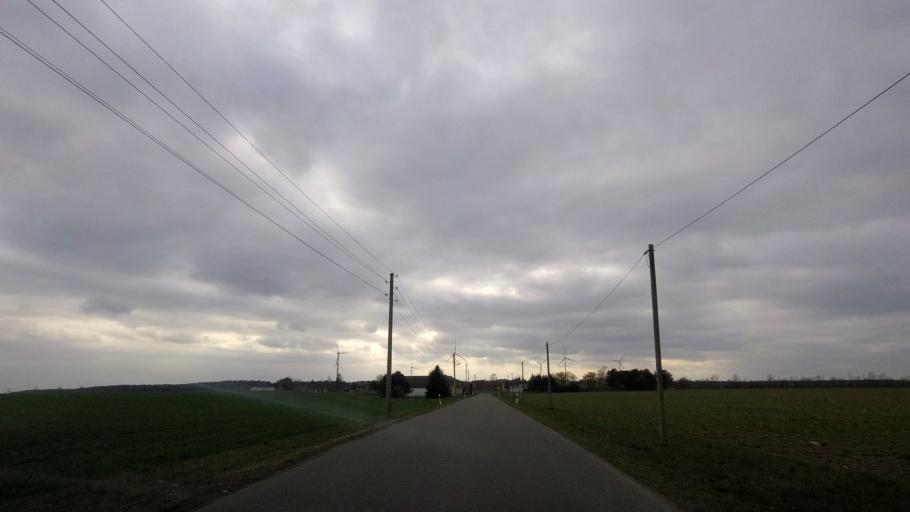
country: DE
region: Saxony-Anhalt
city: Seyda
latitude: 51.9266
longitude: 12.8957
